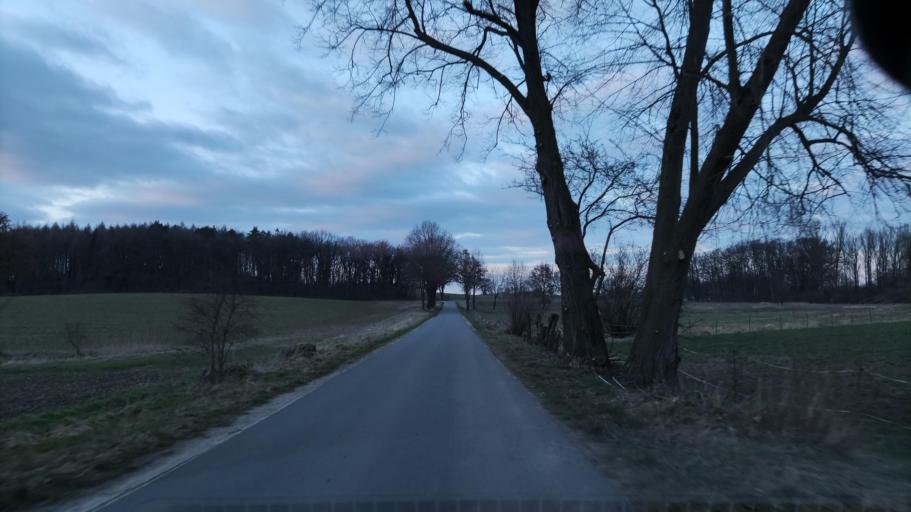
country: DE
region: Lower Saxony
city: Natendorf
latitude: 53.0752
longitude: 10.4410
